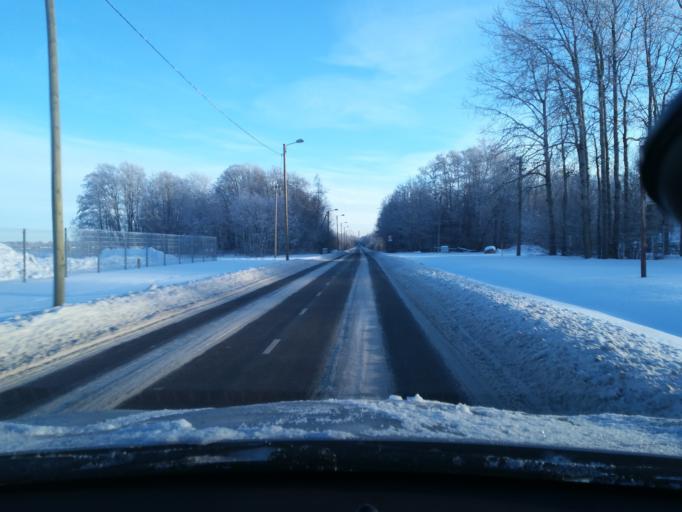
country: EE
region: Harju
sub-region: Saue vald
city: Laagri
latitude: 59.3945
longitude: 24.5976
